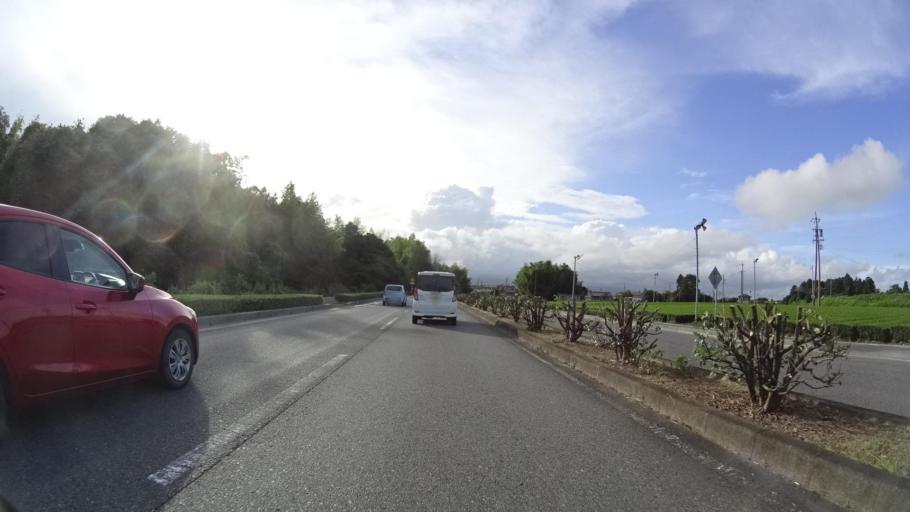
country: JP
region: Mie
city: Kameyama
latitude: 34.8962
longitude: 136.5053
